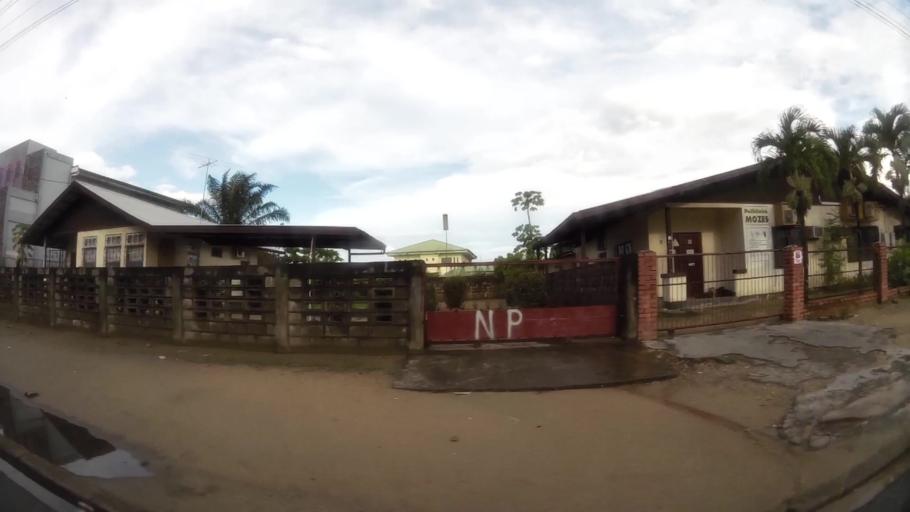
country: SR
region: Paramaribo
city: Paramaribo
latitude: 5.8229
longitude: -55.1825
